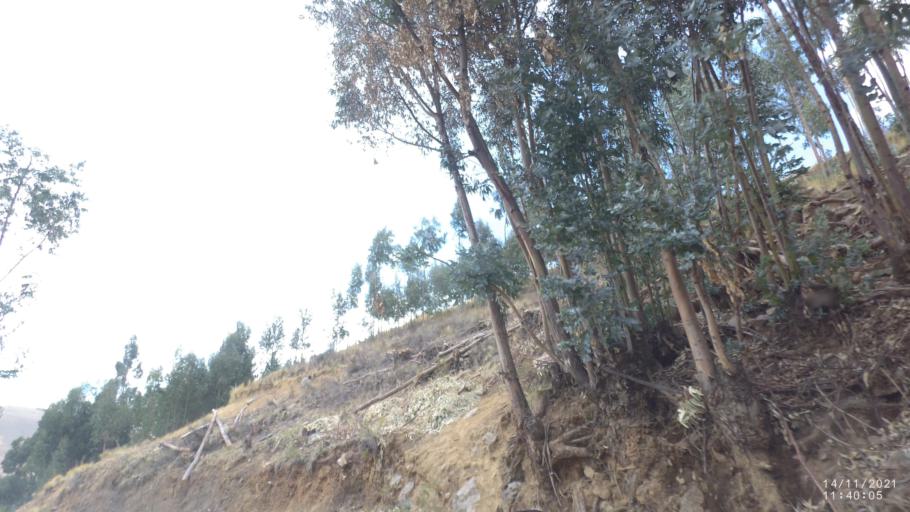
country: BO
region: Cochabamba
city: Colomi
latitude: -17.3510
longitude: -65.9974
